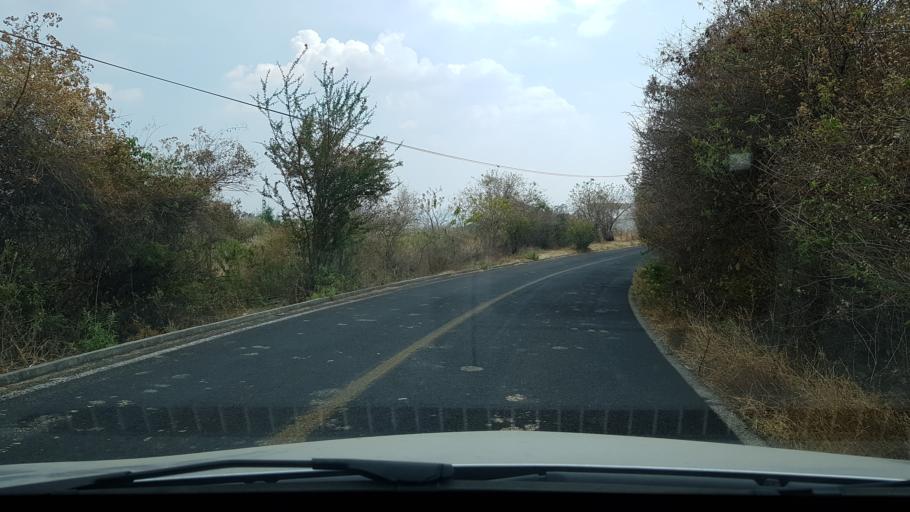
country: MX
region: Morelos
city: Tlacotepec
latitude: 18.8238
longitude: -98.7417
